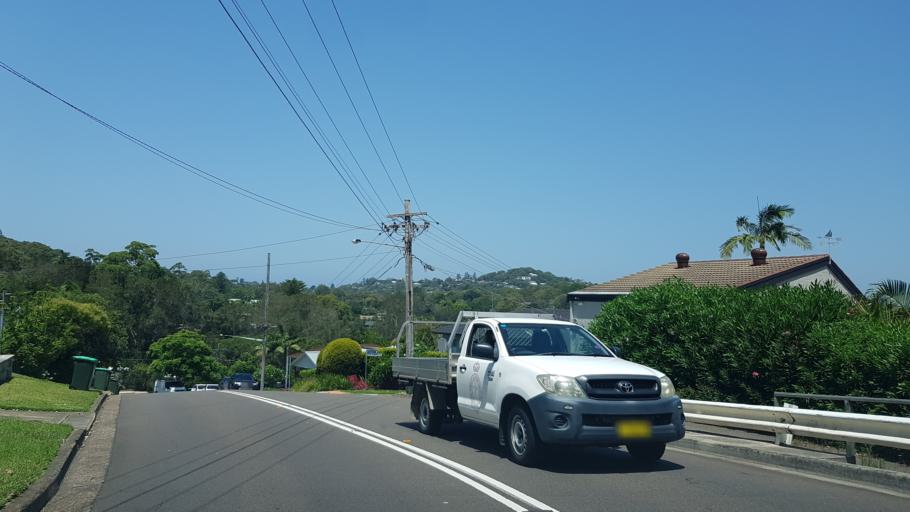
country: AU
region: New South Wales
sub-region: Pittwater
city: Bay View
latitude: -33.6542
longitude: 151.3050
